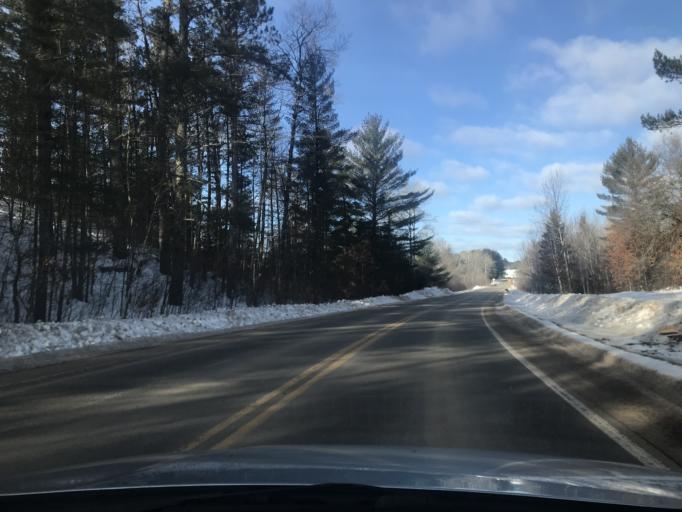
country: US
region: Wisconsin
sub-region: Marinette County
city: Niagara
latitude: 45.6377
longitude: -87.9740
